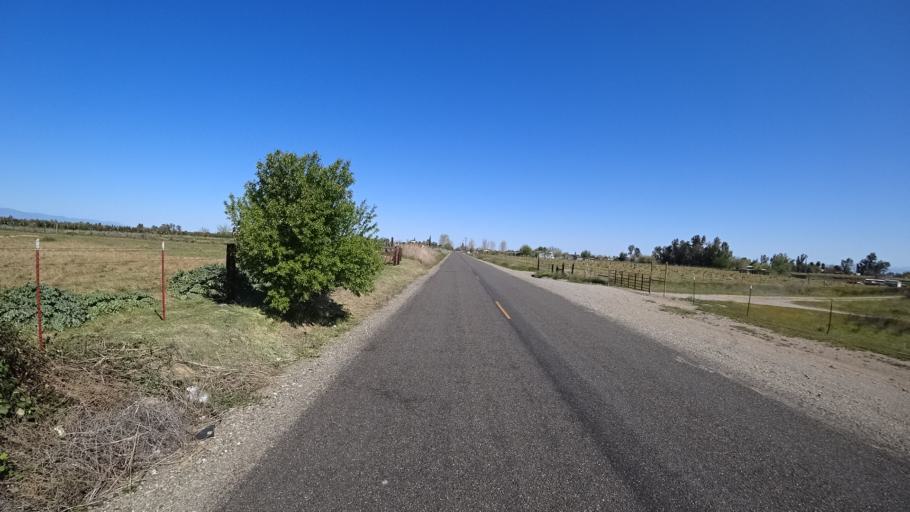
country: US
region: California
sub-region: Glenn County
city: Orland
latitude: 39.7292
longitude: -122.2158
